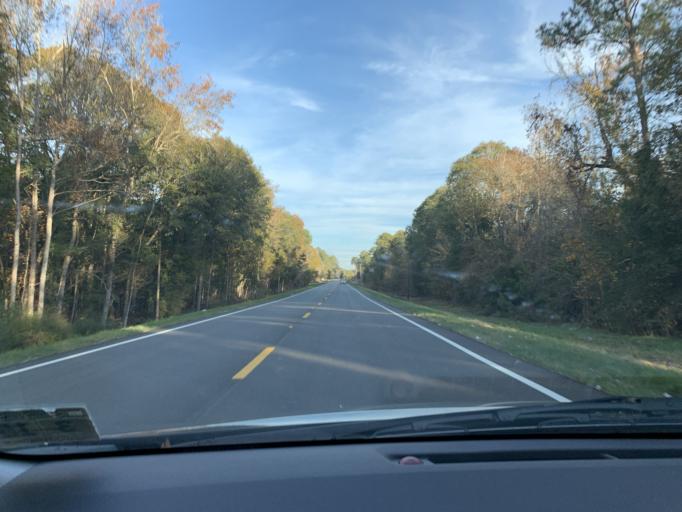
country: US
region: Georgia
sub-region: Irwin County
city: Ocilla
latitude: 31.5955
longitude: -83.1267
